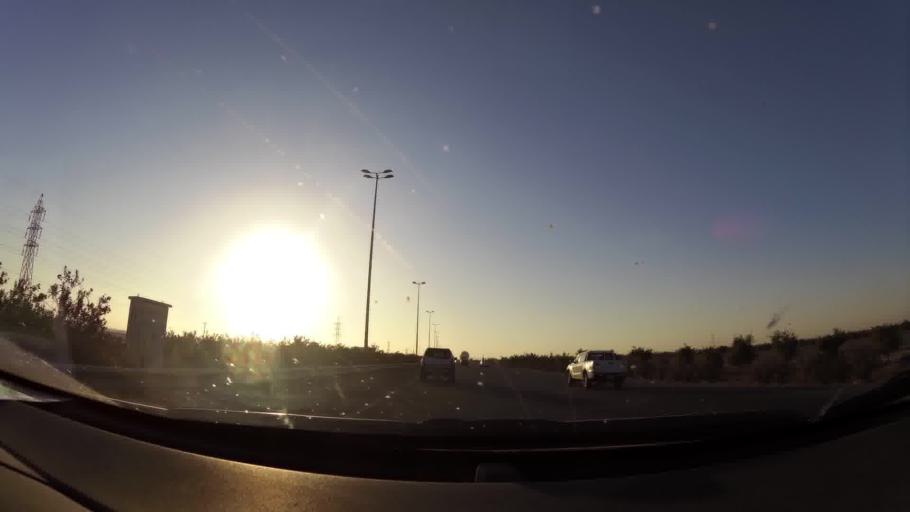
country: KW
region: Al Ahmadi
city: Al Fahahil
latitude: 28.9804
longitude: 48.1552
